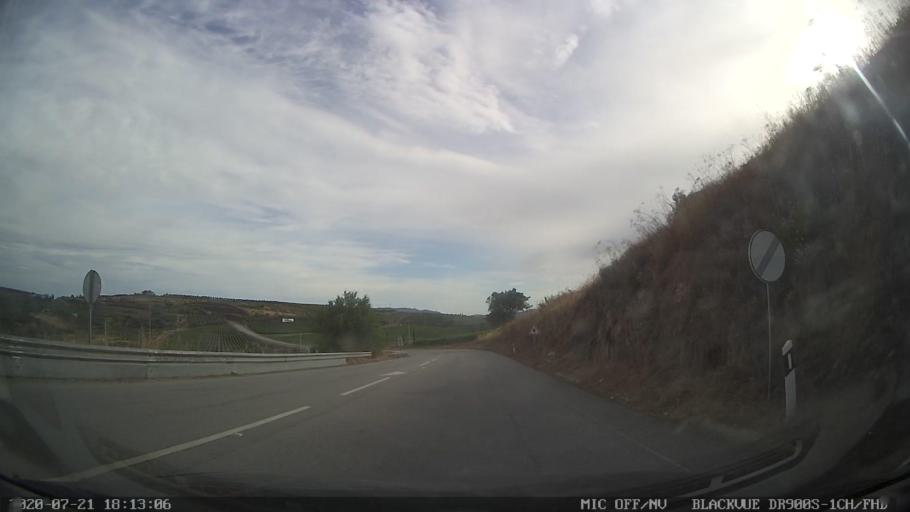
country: PT
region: Viseu
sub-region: Sao Joao da Pesqueira
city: Sao Joao da Pesqueira
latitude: 41.1345
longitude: -7.3982
